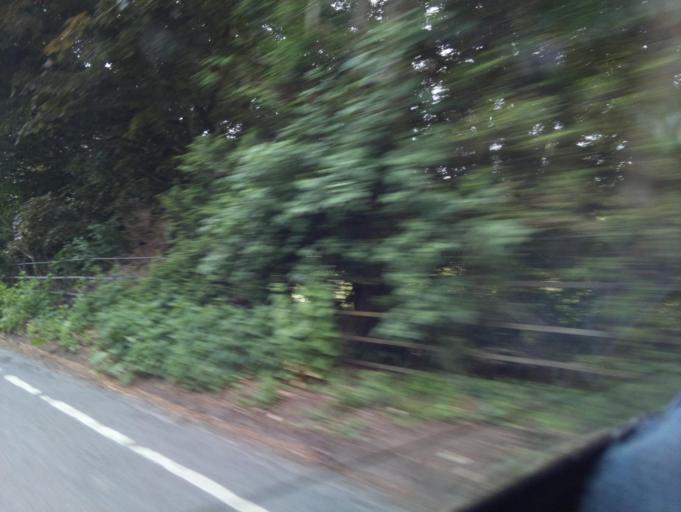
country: GB
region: England
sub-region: Gloucestershire
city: Shurdington
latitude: 51.8484
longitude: -2.0806
